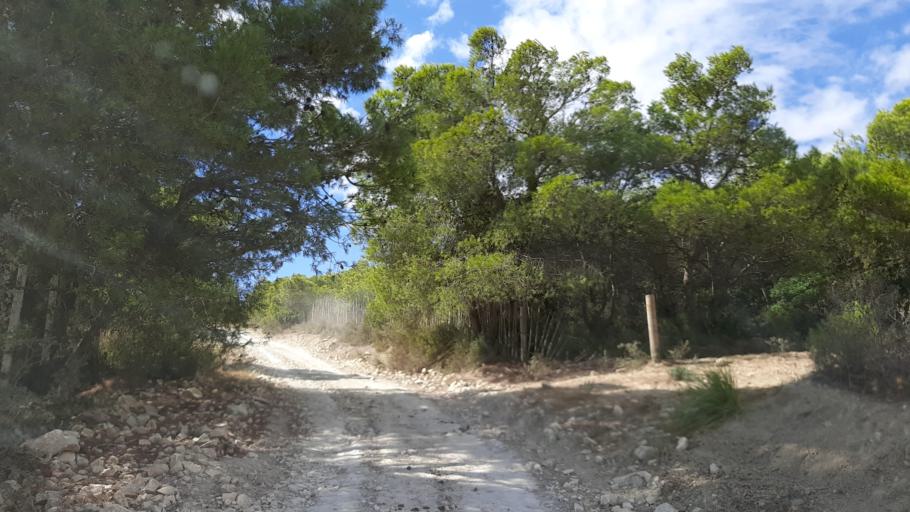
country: TN
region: Zaghwan
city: Zaghouan
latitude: 36.5098
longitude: 10.1838
